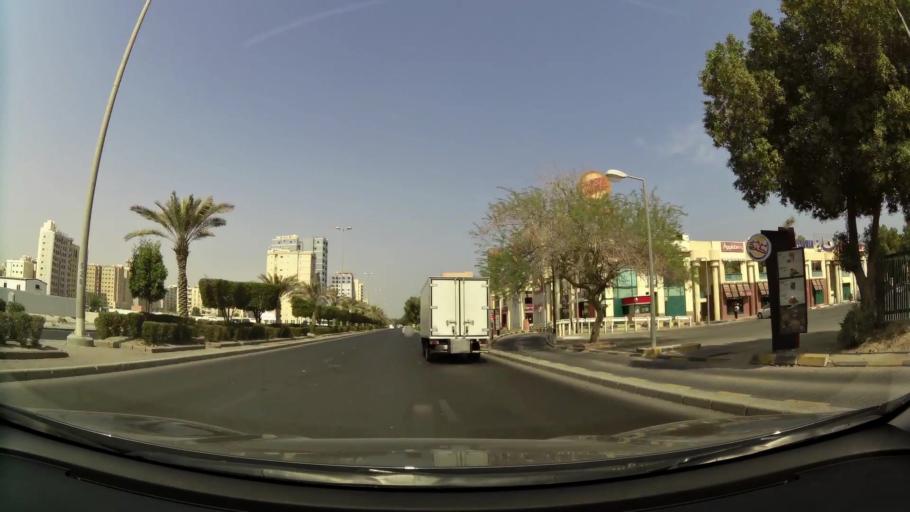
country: KW
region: Al Ahmadi
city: Al Mahbulah
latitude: 29.1393
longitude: 48.1300
